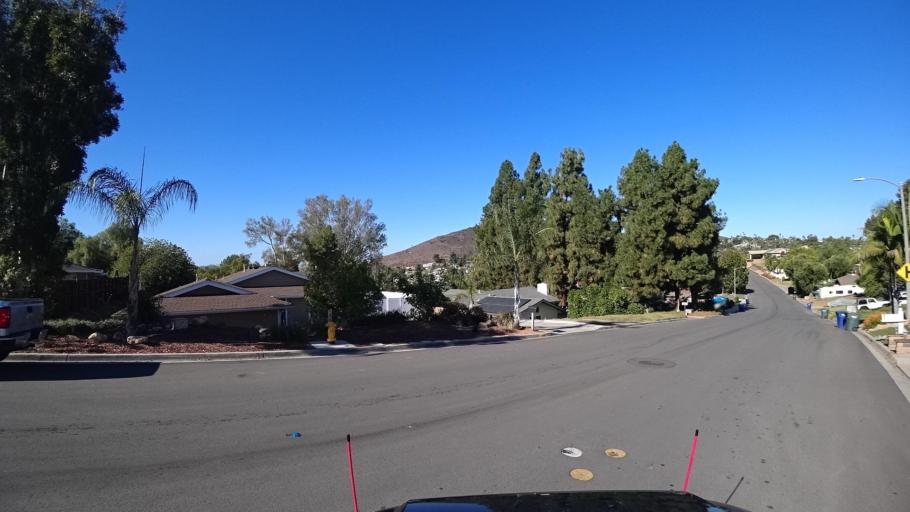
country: US
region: California
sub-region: San Diego County
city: Winter Gardens
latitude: 32.8273
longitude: -116.9278
